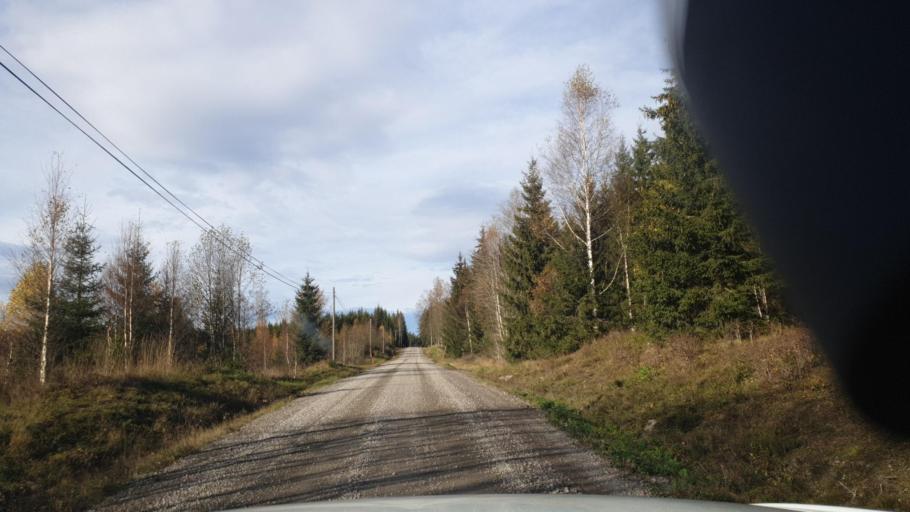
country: SE
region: Vaermland
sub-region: Eda Kommun
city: Charlottenberg
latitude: 59.9734
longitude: 12.4957
